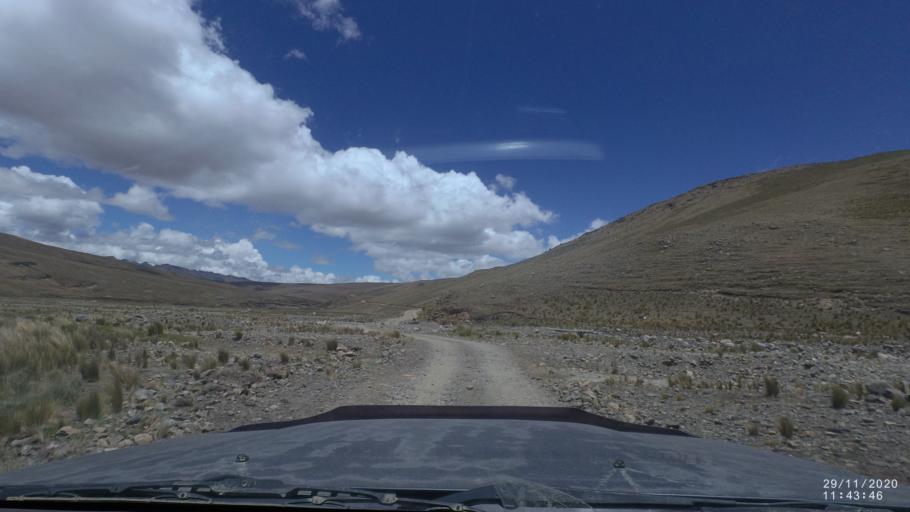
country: BO
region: Cochabamba
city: Cochabamba
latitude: -17.1954
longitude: -66.2443
